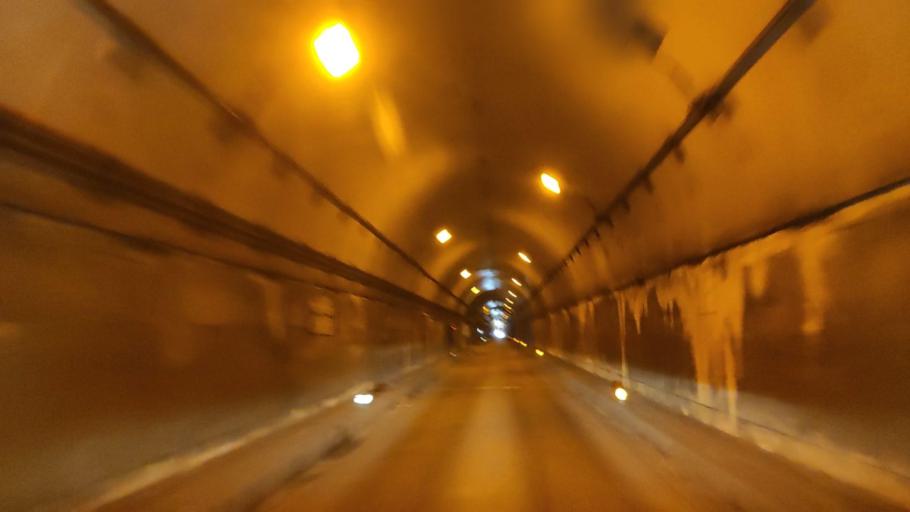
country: JP
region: Gifu
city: Gifu-shi
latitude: 35.4198
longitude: 136.7729
